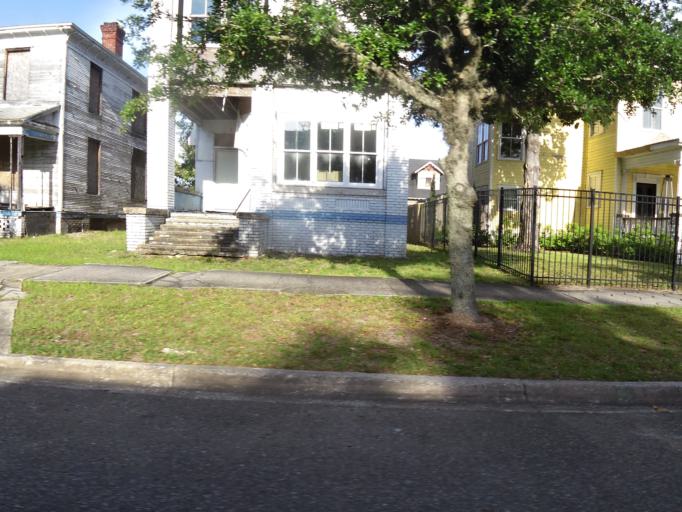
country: US
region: Florida
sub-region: Duval County
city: Jacksonville
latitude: 30.3395
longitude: -81.6562
